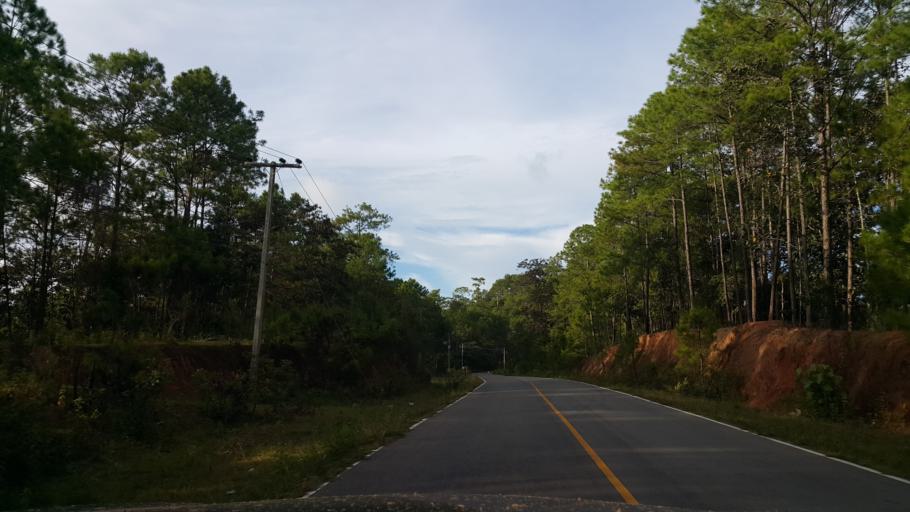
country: TH
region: Chiang Mai
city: Chaem Luang
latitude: 19.0848
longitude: 98.3382
